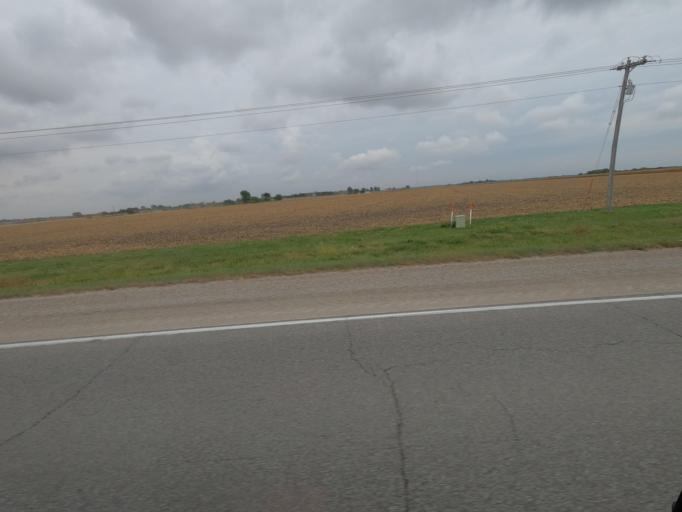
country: US
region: Iowa
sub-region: Wapello County
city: Ottumwa
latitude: 40.9480
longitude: -92.2270
